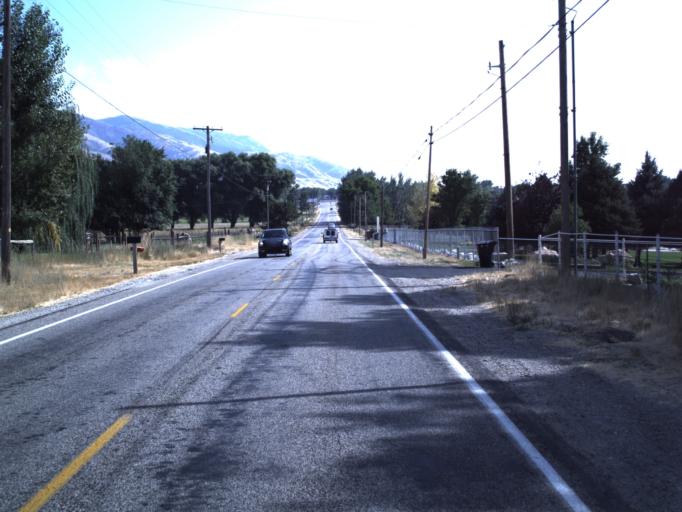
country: US
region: Utah
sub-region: Box Elder County
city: Brigham City
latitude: 41.5410
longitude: -112.0153
